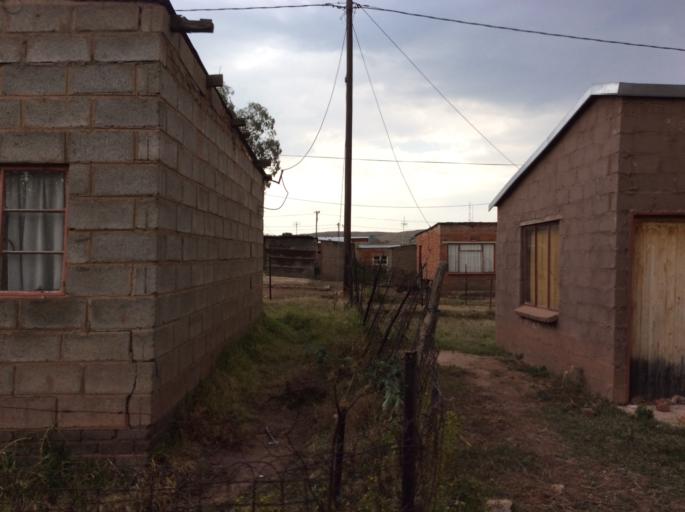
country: ZA
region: Orange Free State
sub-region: Xhariep District Municipality
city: Dewetsdorp
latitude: -29.5848
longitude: 26.6734
